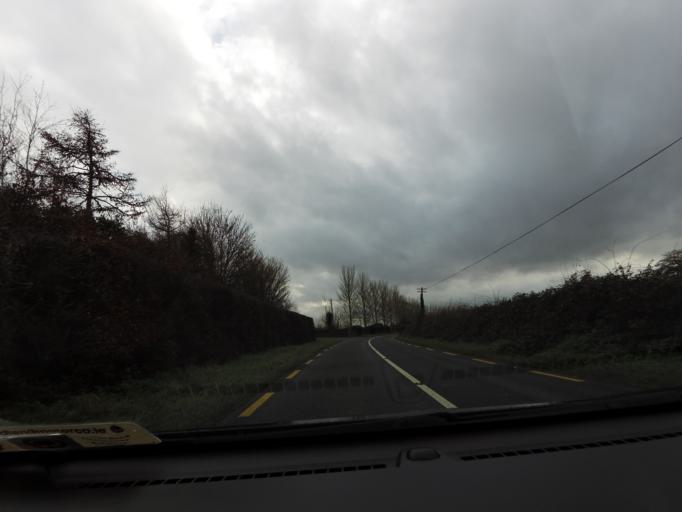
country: IE
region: Leinster
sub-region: Kilkenny
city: Kilkenny
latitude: 52.7025
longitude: -7.2688
